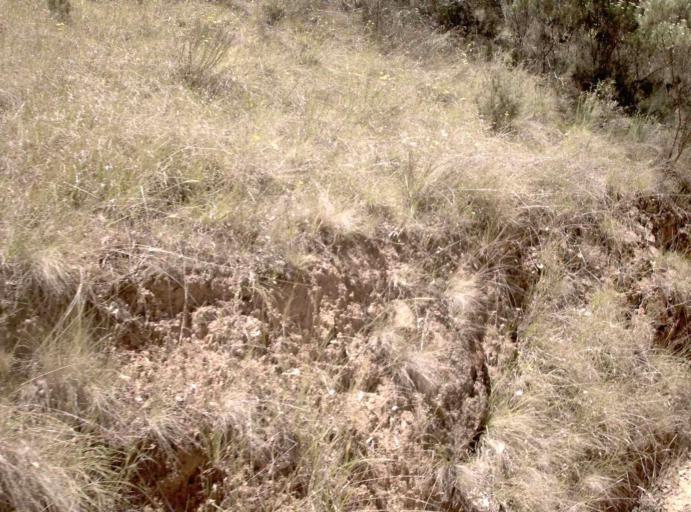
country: AU
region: New South Wales
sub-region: Snowy River
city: Jindabyne
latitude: -36.9316
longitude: 148.3563
